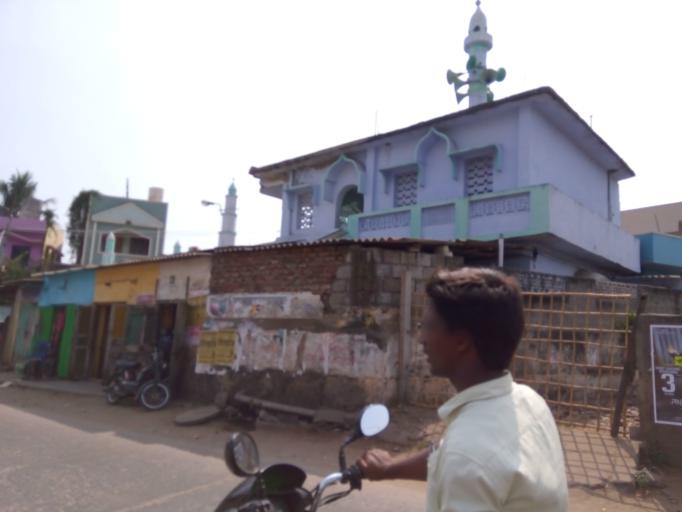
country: IN
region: Andhra Pradesh
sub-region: Prakasam
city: Chirala
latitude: 15.8359
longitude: 80.3635
